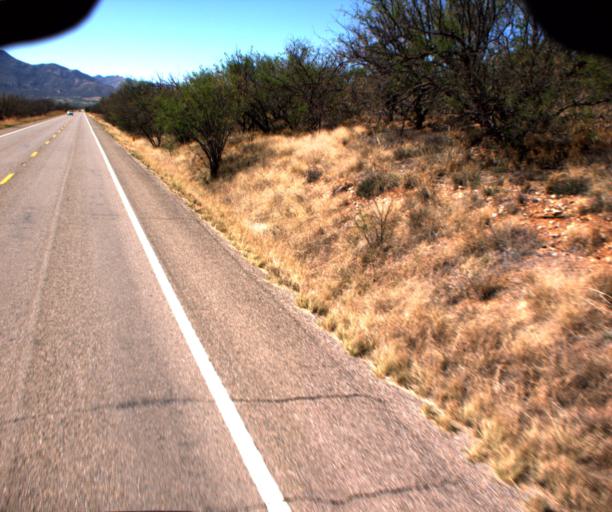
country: US
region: Arizona
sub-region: Santa Cruz County
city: Rio Rico
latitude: 31.5874
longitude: -110.7269
